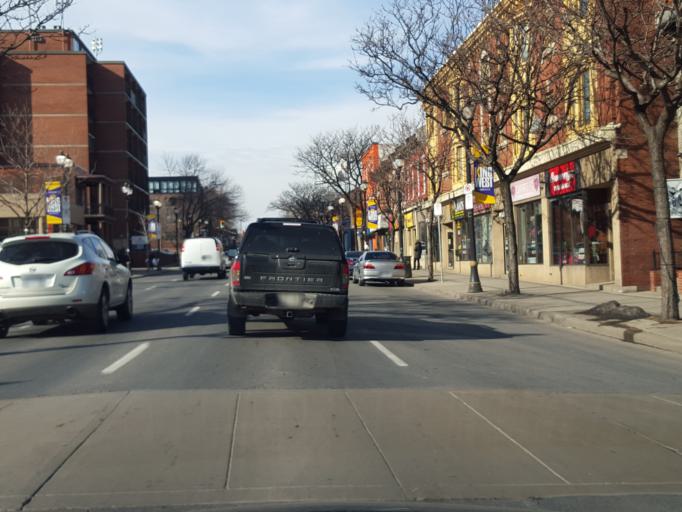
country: CA
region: Ontario
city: Hamilton
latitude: 43.2586
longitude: -79.8758
